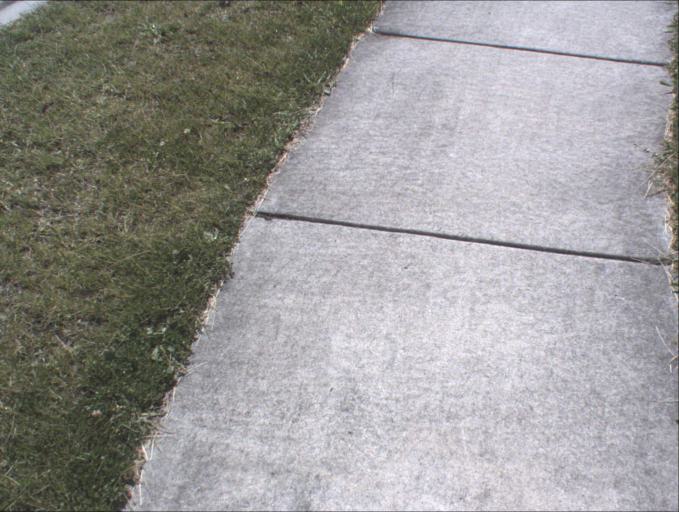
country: AU
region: Queensland
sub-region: Logan
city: Woodridge
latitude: -27.6587
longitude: 153.0803
